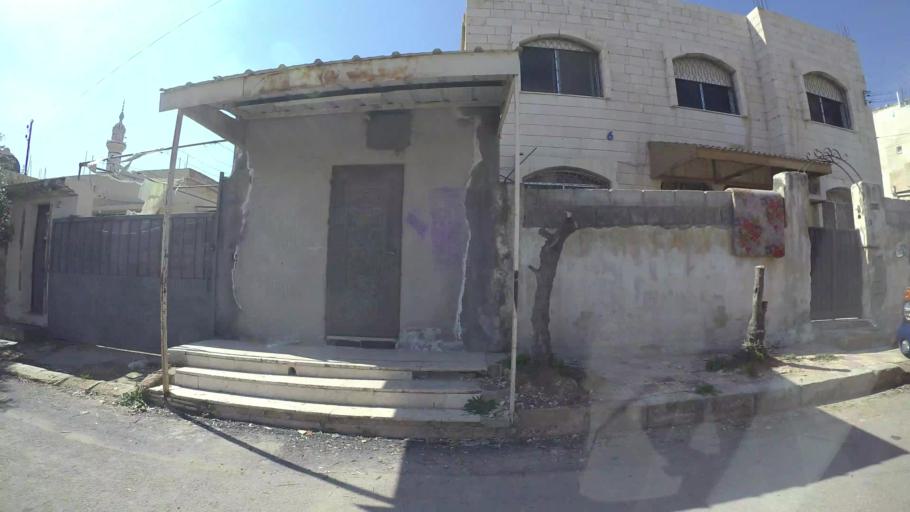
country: JO
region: Amman
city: Al Bunayyat ash Shamaliyah
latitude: 31.9040
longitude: 35.8998
